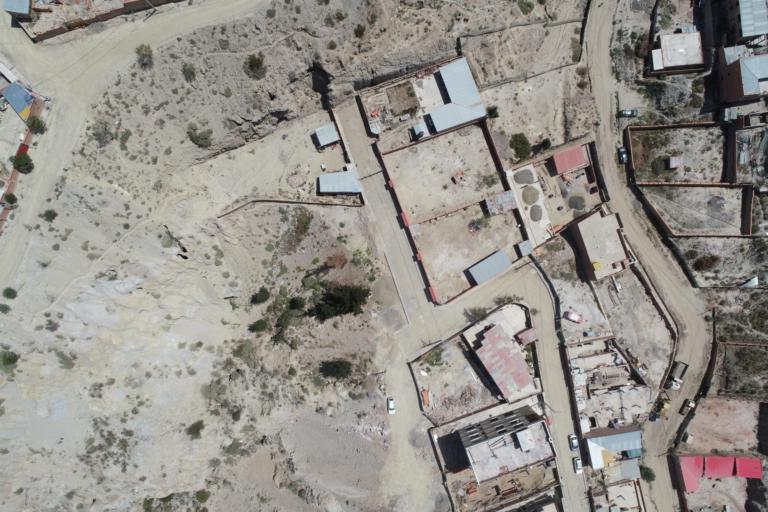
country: BO
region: La Paz
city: La Paz
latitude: -16.5373
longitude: -68.1047
